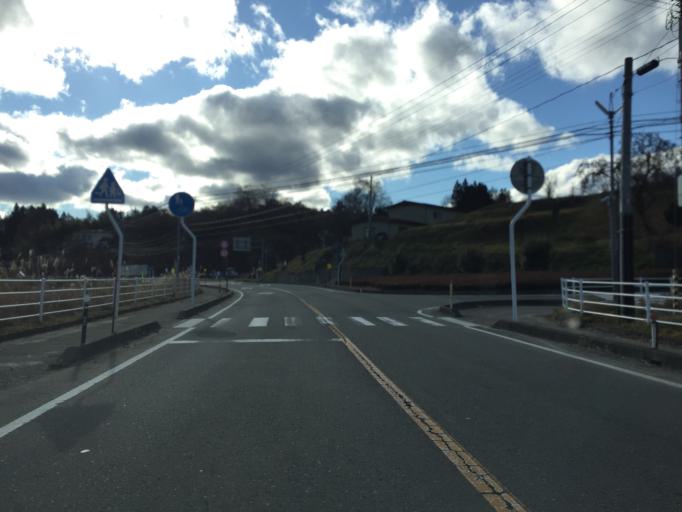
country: JP
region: Fukushima
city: Nihommatsu
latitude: 37.5942
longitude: 140.5786
